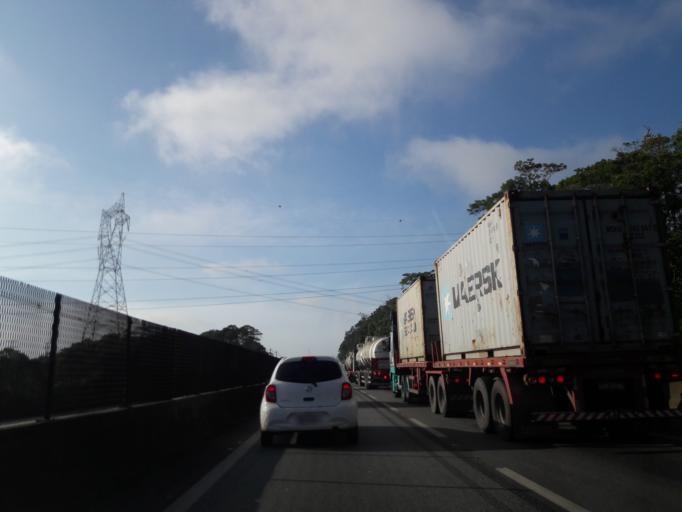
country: BR
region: Sao Paulo
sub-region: Cubatao
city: Cubatao
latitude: -23.8490
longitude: -46.5047
